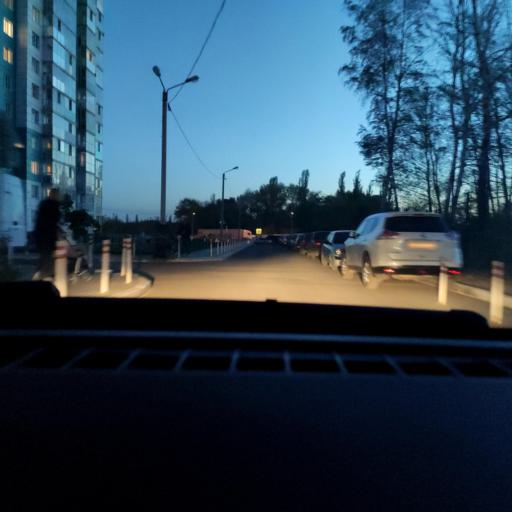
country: RU
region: Voronezj
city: Maslovka
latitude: 51.6350
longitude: 39.2929
